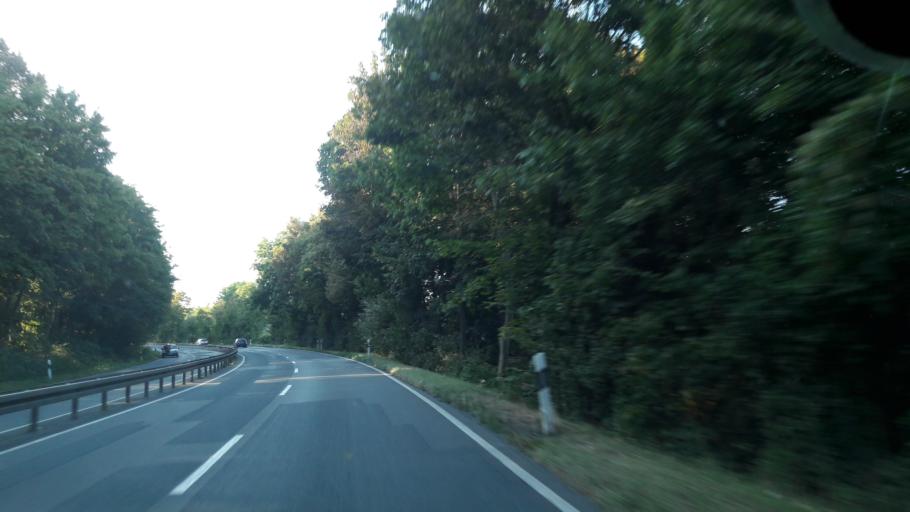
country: DE
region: Lower Saxony
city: Hildesheim
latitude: 52.1694
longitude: 9.9571
